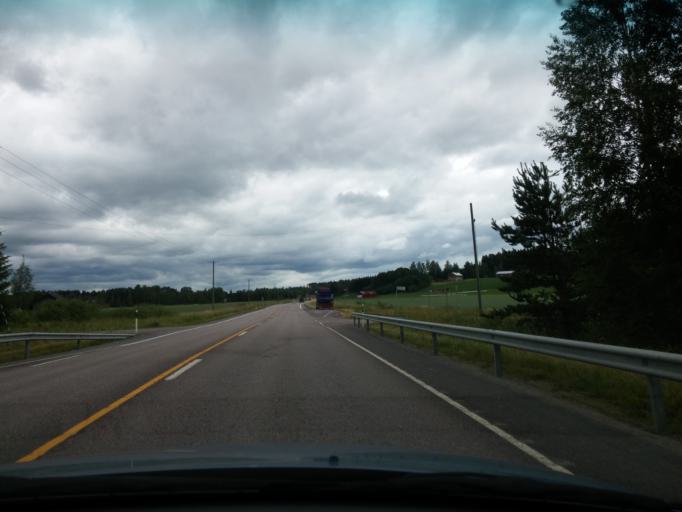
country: FI
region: Uusimaa
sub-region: Porvoo
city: Askola
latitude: 60.4529
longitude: 25.5833
